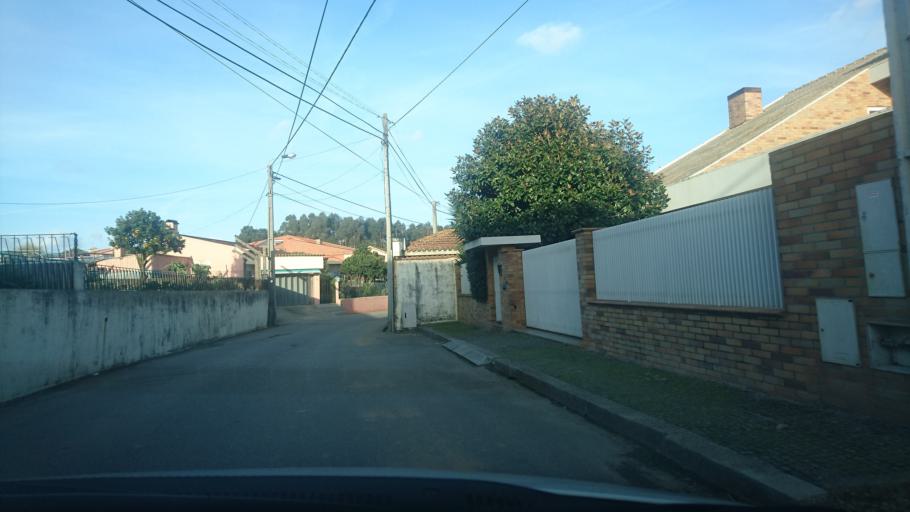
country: PT
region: Aveiro
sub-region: Espinho
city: Souto
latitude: 40.9972
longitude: -8.6083
